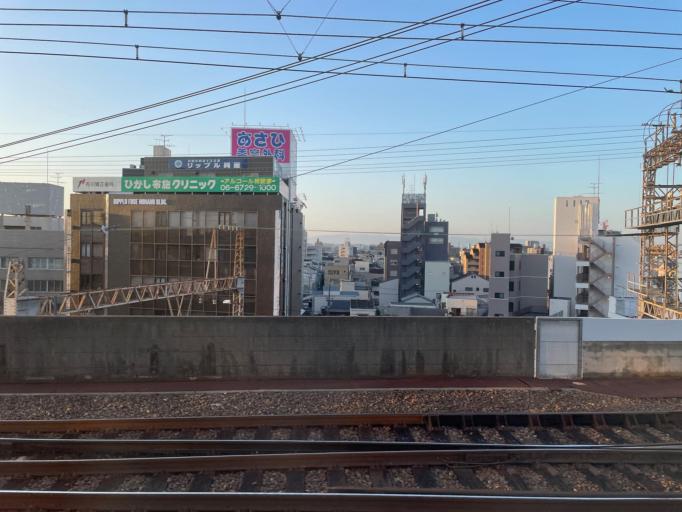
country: JP
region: Osaka
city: Yao
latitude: 34.6642
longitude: 135.5656
